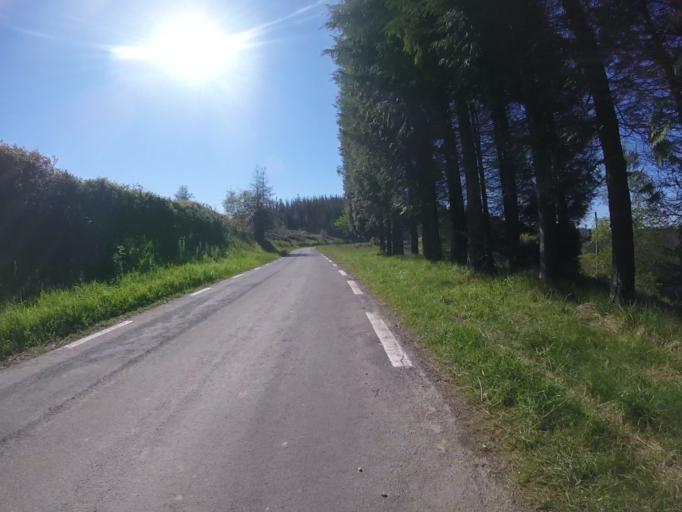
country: ES
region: Basque Country
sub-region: Provincia de Guipuzcoa
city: Aizarnazabal
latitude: 43.2126
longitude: -2.2025
